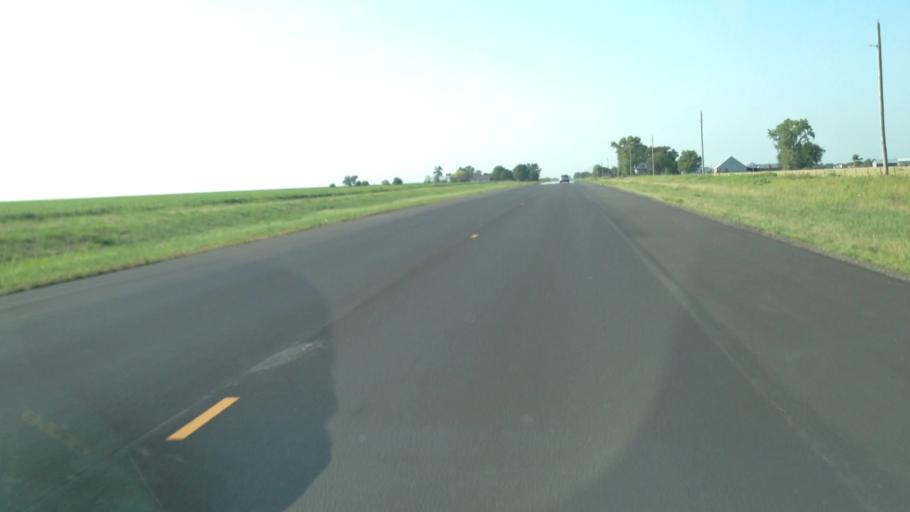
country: US
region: Kansas
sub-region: Anderson County
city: Garnett
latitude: 38.4205
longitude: -95.2486
